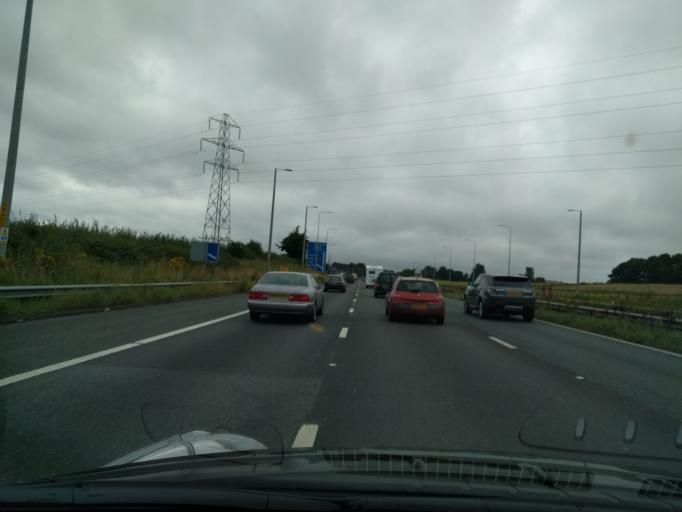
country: GB
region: England
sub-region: Warrington
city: Winwick
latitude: 53.4362
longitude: -2.5760
